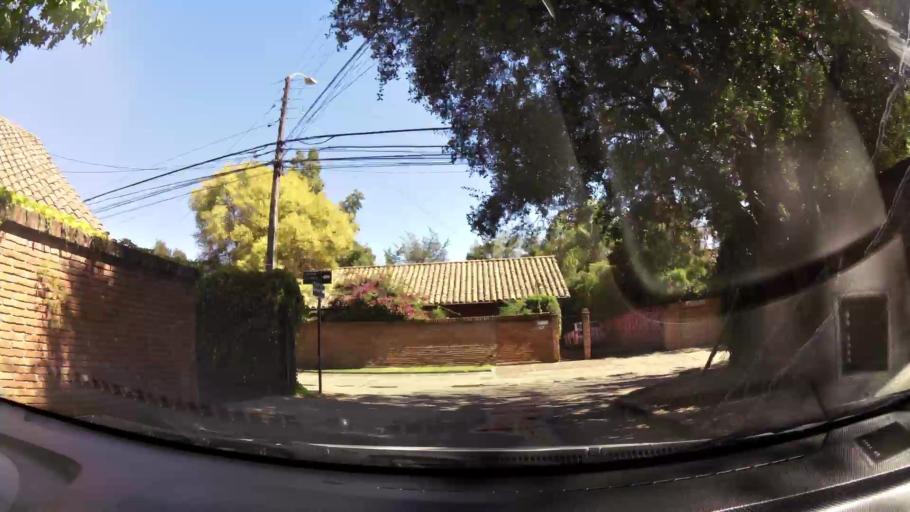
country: CL
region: Maule
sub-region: Provincia de Talca
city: Talca
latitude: -35.4333
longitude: -71.6186
